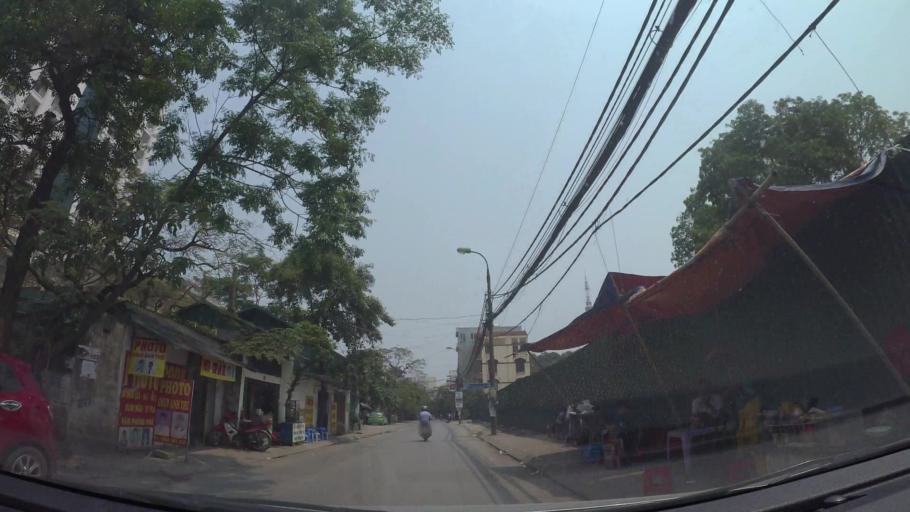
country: VN
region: Ha Noi
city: Thanh Xuan
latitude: 20.9963
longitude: 105.7885
